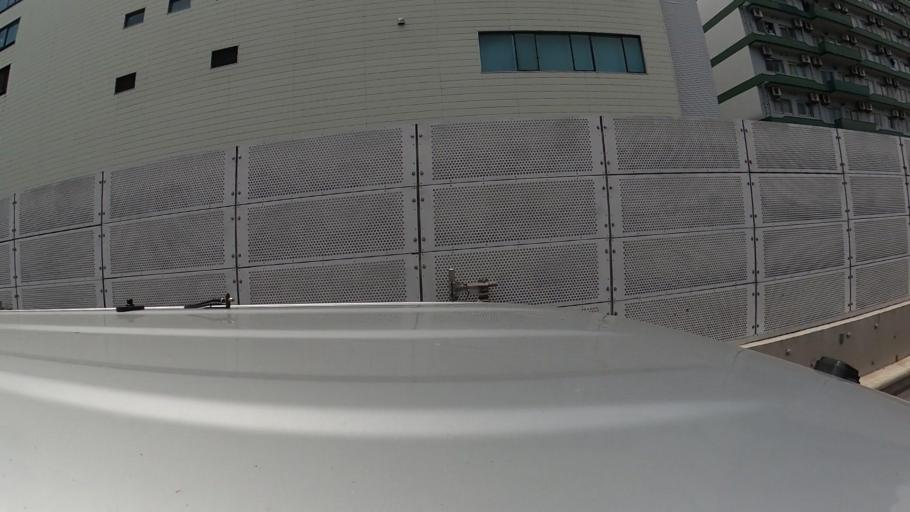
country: JP
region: Tokyo
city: Tokyo
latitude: 35.6445
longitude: 139.7559
